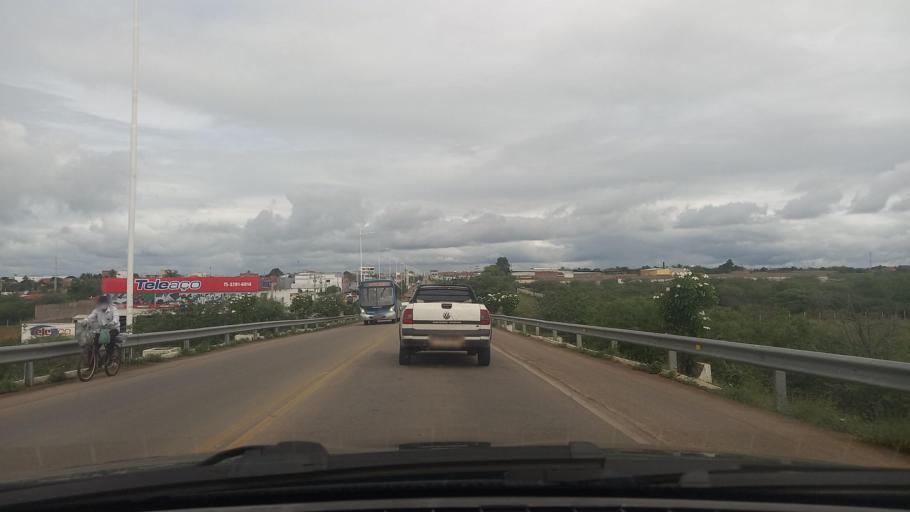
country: BR
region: Bahia
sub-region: Paulo Afonso
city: Paulo Afonso
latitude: -9.4356
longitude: -38.2259
